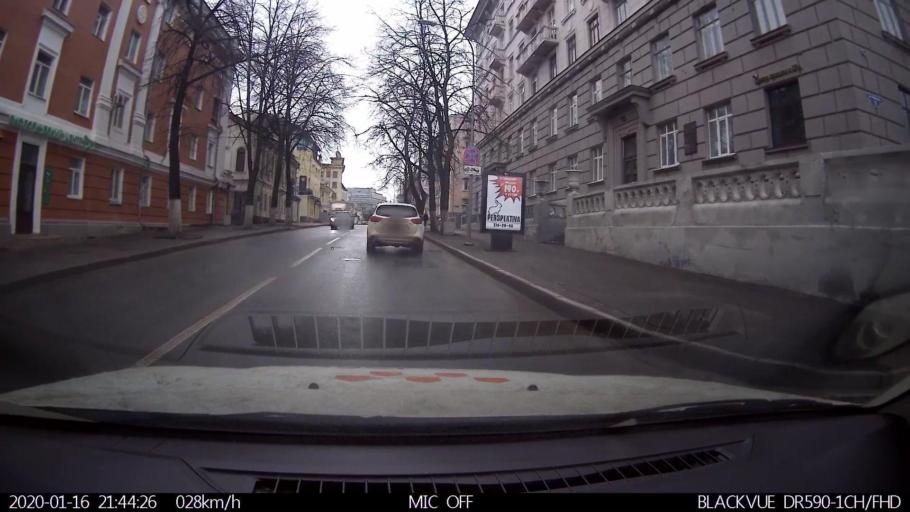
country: RU
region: Nizjnij Novgorod
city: Nizhniy Novgorod
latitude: 56.3302
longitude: 44.0075
